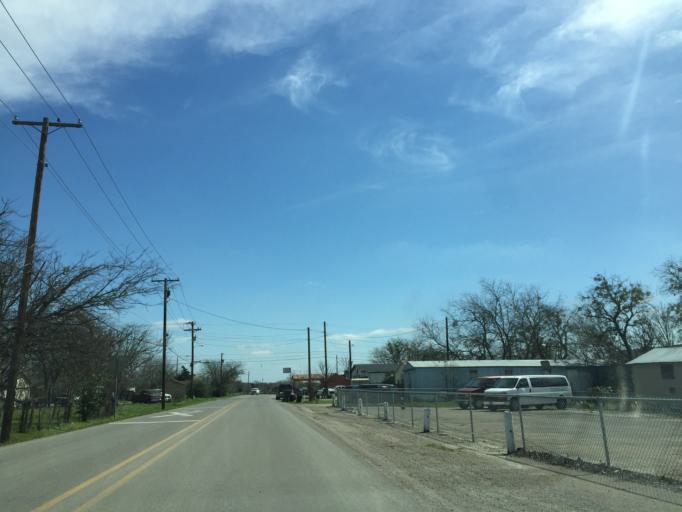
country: US
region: Texas
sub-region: Williamson County
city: Taylor
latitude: 30.5653
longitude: -97.4031
